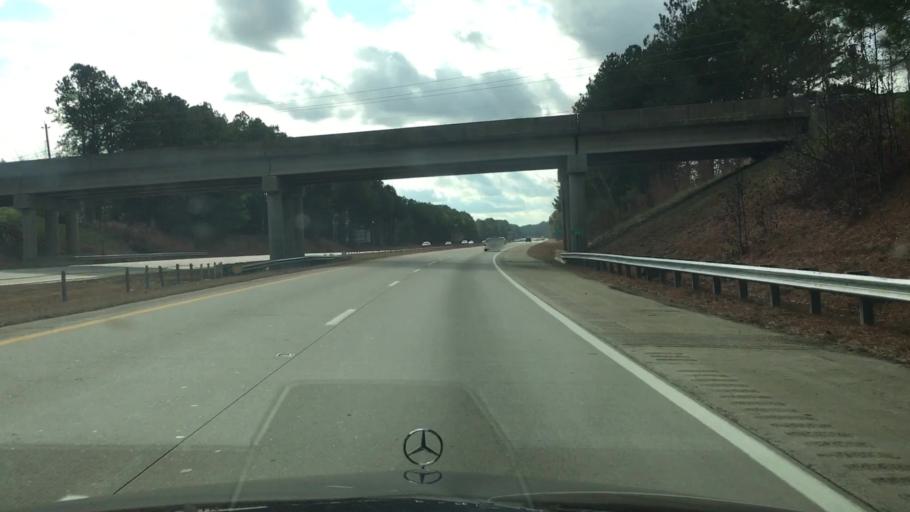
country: US
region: North Carolina
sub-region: Johnston County
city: Clayton
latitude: 35.5985
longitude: -78.5649
